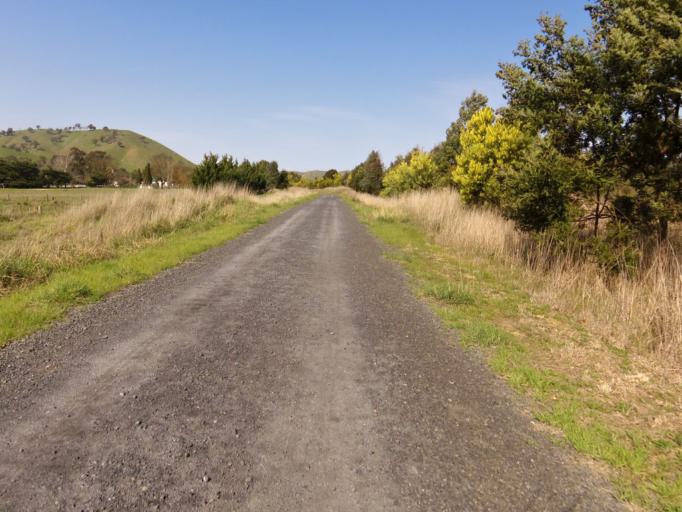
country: AU
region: Victoria
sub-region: Murrindindi
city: Alexandra
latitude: -37.0163
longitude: 145.7945
